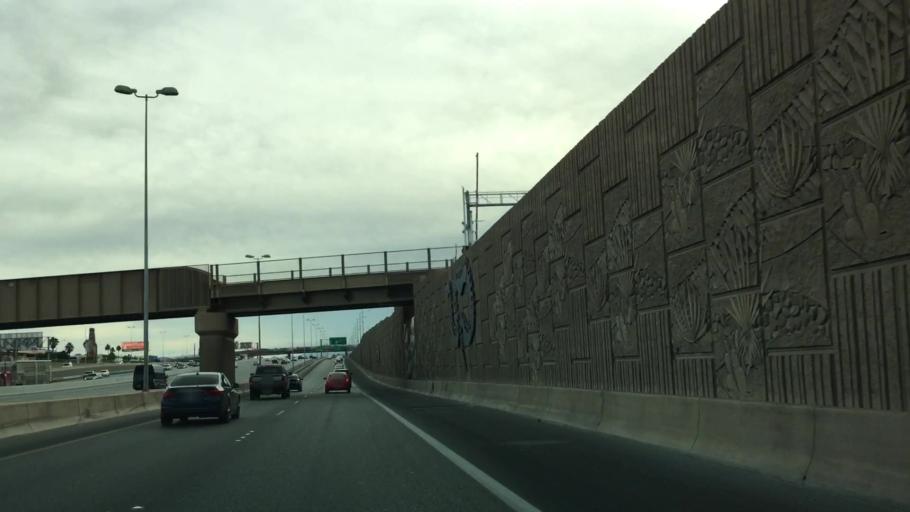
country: US
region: Nevada
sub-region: Clark County
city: Paradise
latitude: 36.0773
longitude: -115.1812
